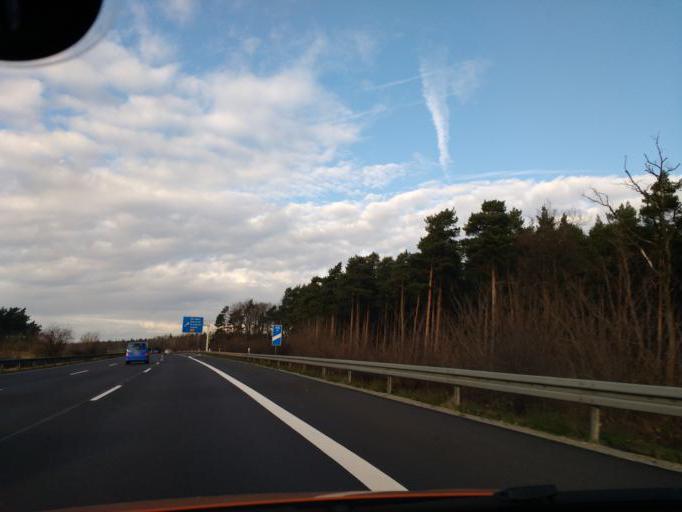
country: DE
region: Lower Saxony
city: Mariental
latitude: 52.2616
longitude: 10.9882
